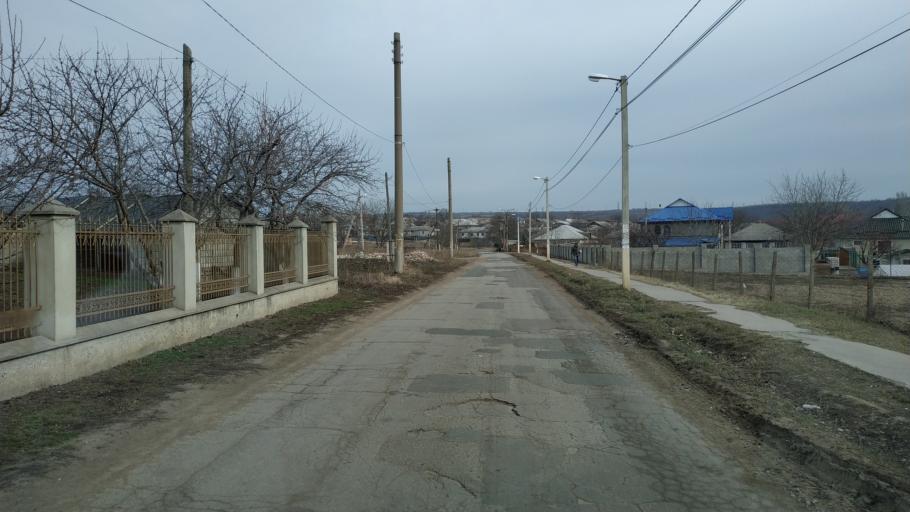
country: MD
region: Chisinau
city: Vatra
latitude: 47.0930
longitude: 28.7606
